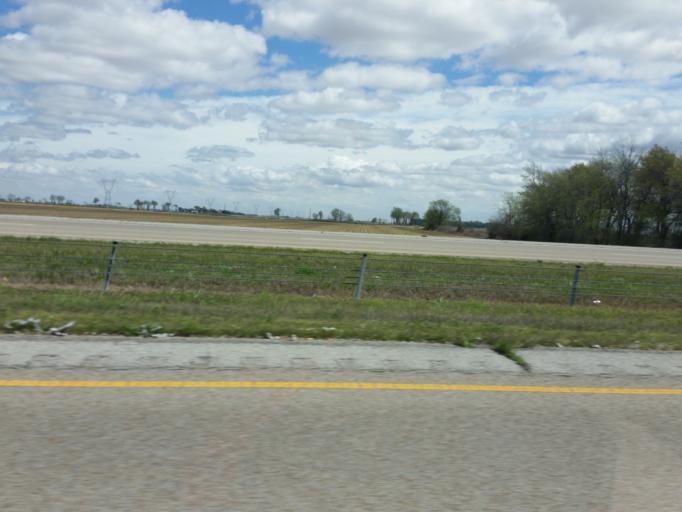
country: US
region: Arkansas
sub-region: Craighead County
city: Bay
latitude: 35.7671
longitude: -90.5772
